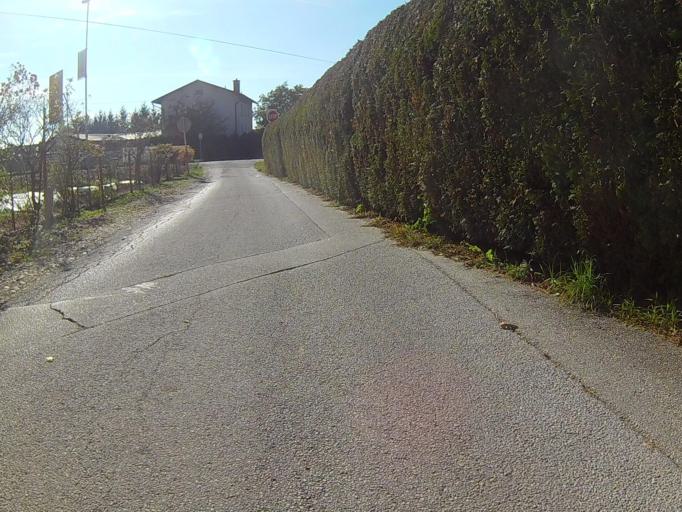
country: SI
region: Ptuj
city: Ptuj
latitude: 46.4296
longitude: 15.8876
